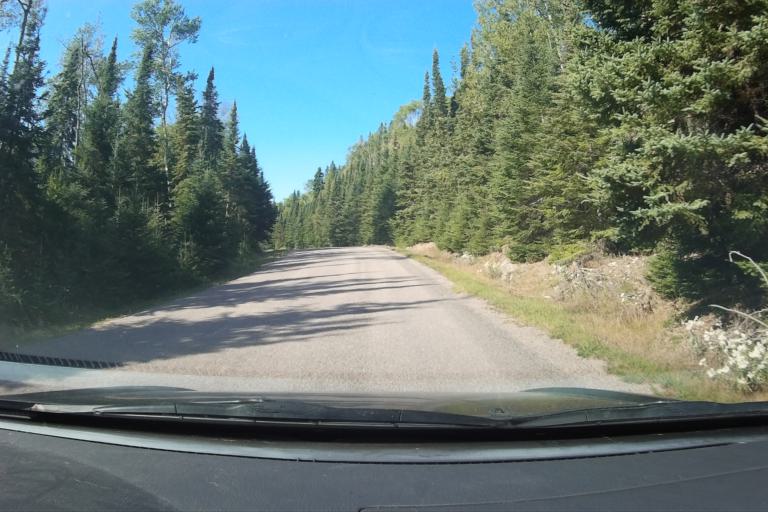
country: CA
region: Ontario
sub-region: Thunder Bay District
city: Thunder Bay
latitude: 48.3435
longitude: -88.8164
